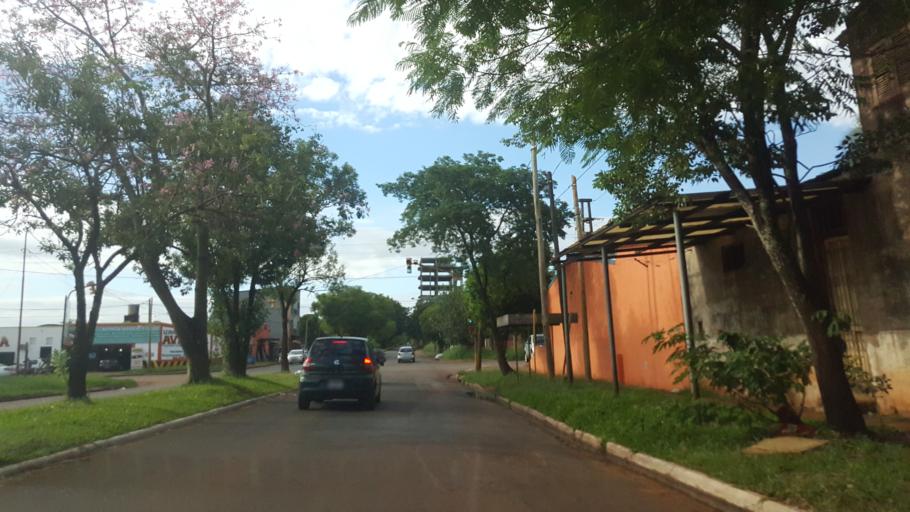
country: AR
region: Misiones
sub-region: Departamento de Capital
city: Posadas
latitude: -27.3745
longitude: -55.9327
